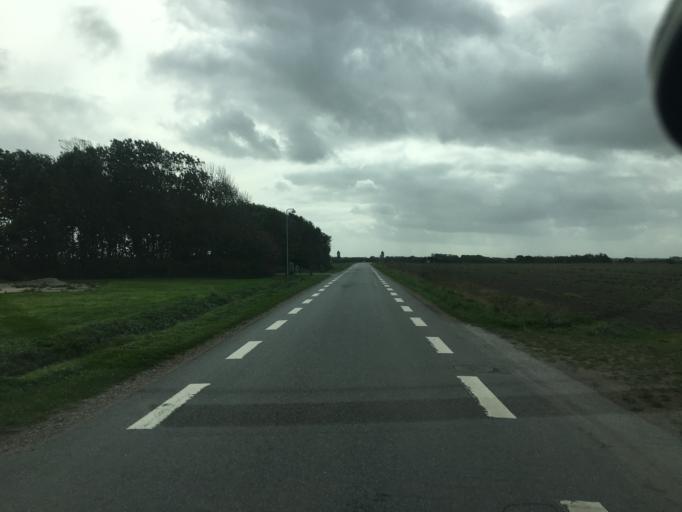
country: DE
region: Schleswig-Holstein
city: Aventoft
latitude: 54.9633
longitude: 8.7658
